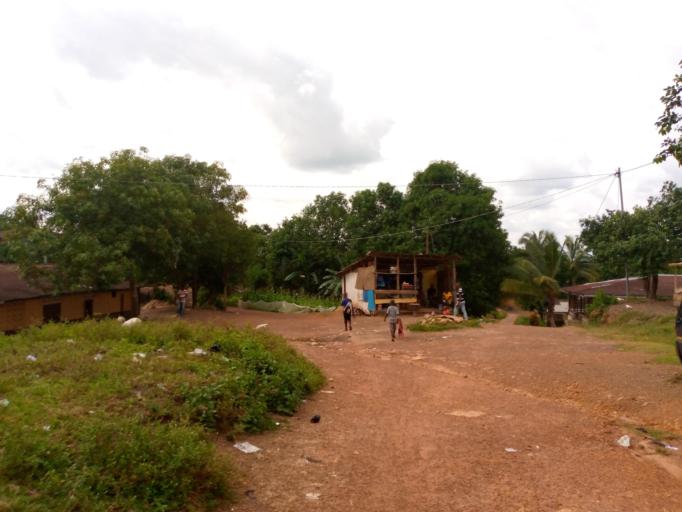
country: SL
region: Northern Province
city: Magburaka
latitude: 8.7239
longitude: -11.9427
